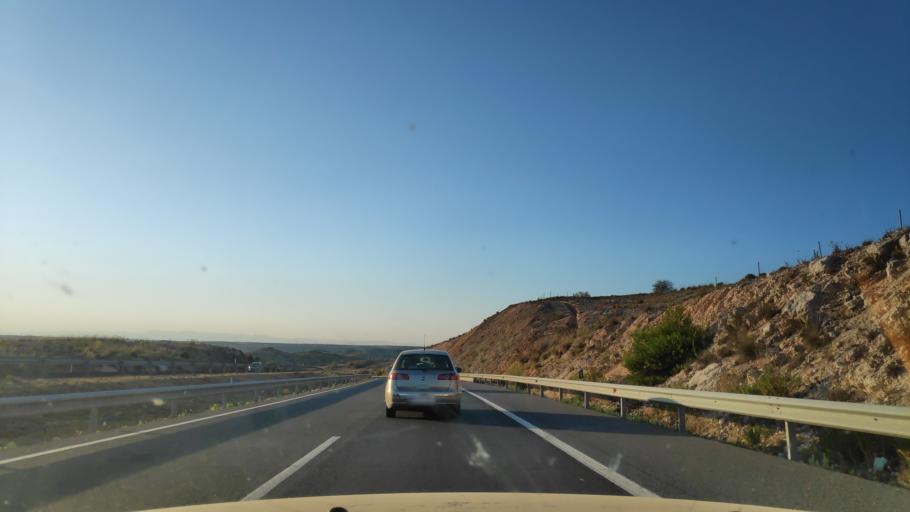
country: ES
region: Madrid
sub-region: Provincia de Madrid
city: Villarejo de Salvanes
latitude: 40.1896
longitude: -3.2989
